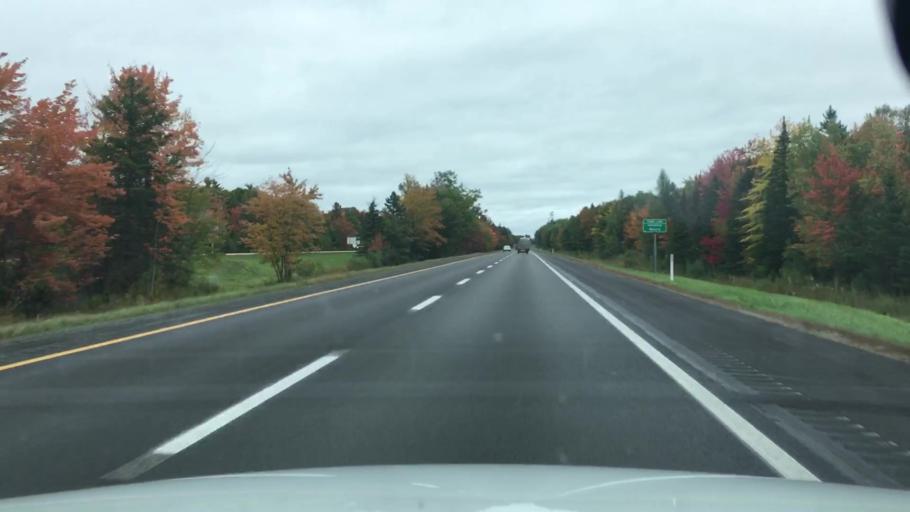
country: US
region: Maine
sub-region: Penobscot County
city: Veazie
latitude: 44.8479
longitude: -68.7287
